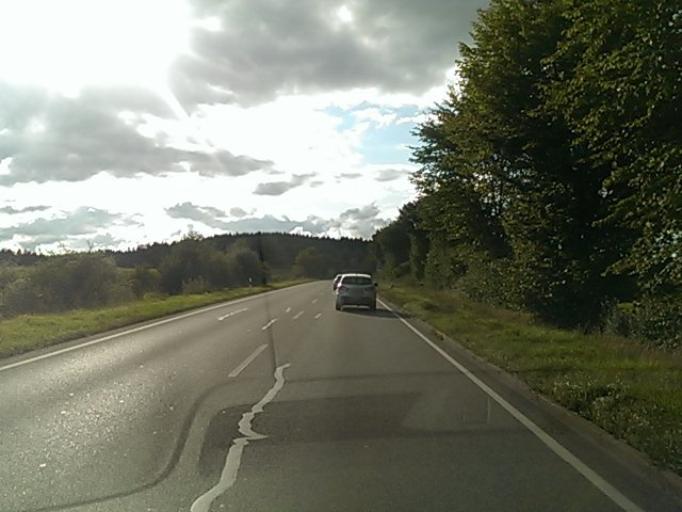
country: DE
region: Baden-Wuerttemberg
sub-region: Freiburg Region
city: Rottweil
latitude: 48.1496
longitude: 8.6200
